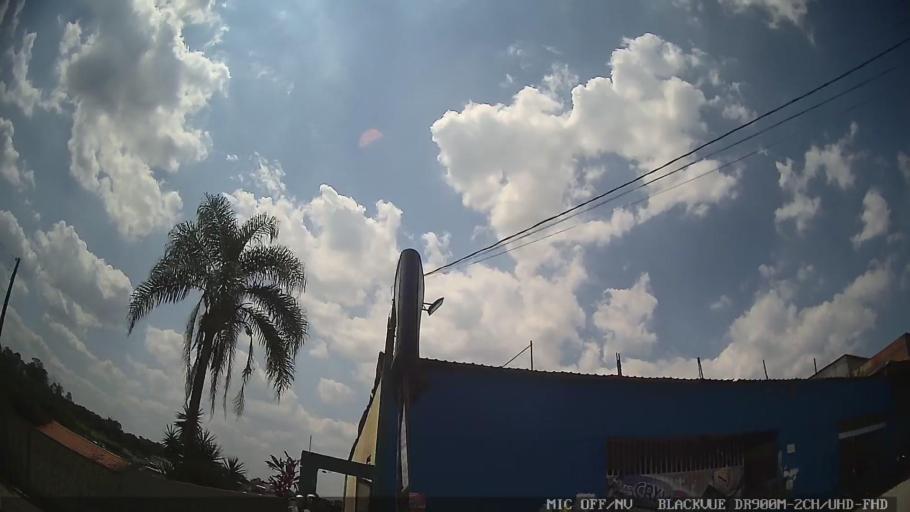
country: BR
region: Sao Paulo
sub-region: Itapecerica Da Serra
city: Itapecerica da Serra
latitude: -23.6871
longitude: -46.8046
